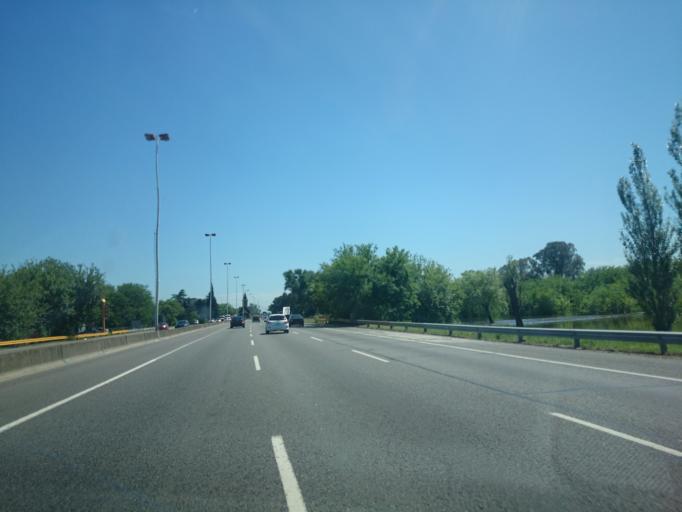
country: AR
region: Buenos Aires
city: San Justo
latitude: -34.7521
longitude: -58.5228
